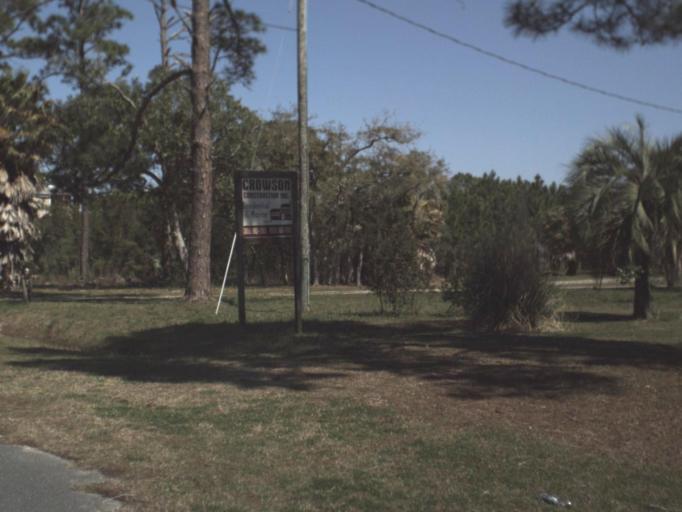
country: US
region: Florida
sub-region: Franklin County
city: Carrabelle
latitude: 29.8738
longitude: -84.6071
